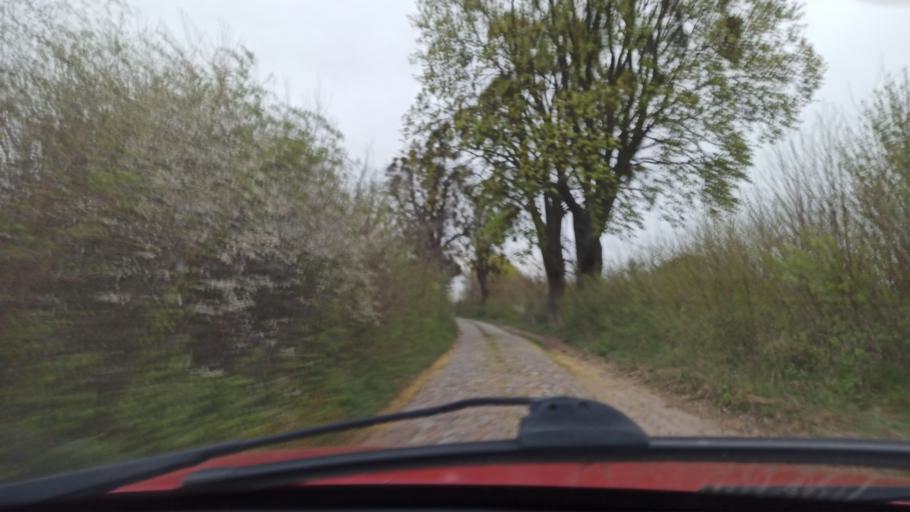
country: PL
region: Kujawsko-Pomorskie
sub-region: Powiat grudziadzki
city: Lasin
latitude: 53.5782
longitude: 19.0899
